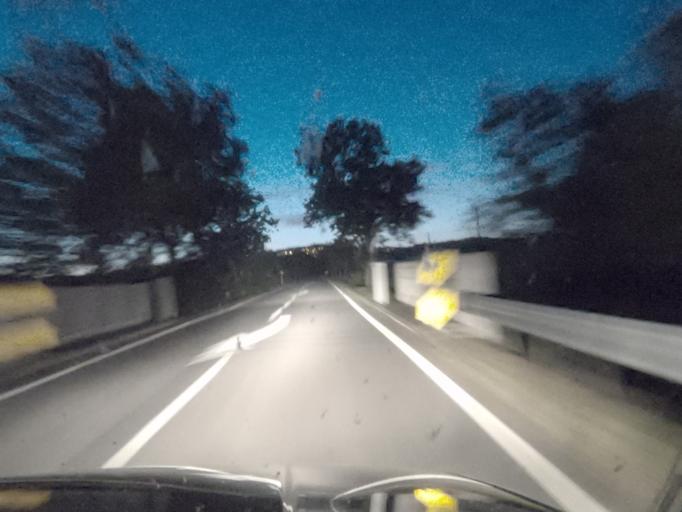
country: PT
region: Castelo Branco
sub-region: Idanha-A-Nova
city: Idanha-a-Nova
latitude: 39.9006
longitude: -7.2122
